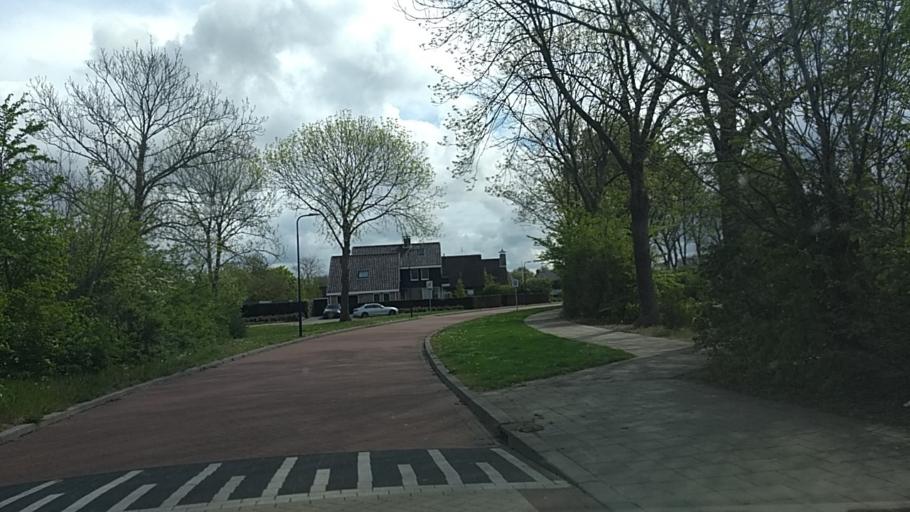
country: NL
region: Friesland
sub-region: Gemeente Harlingen
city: Harlingen
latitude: 53.1706
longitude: 5.4334
